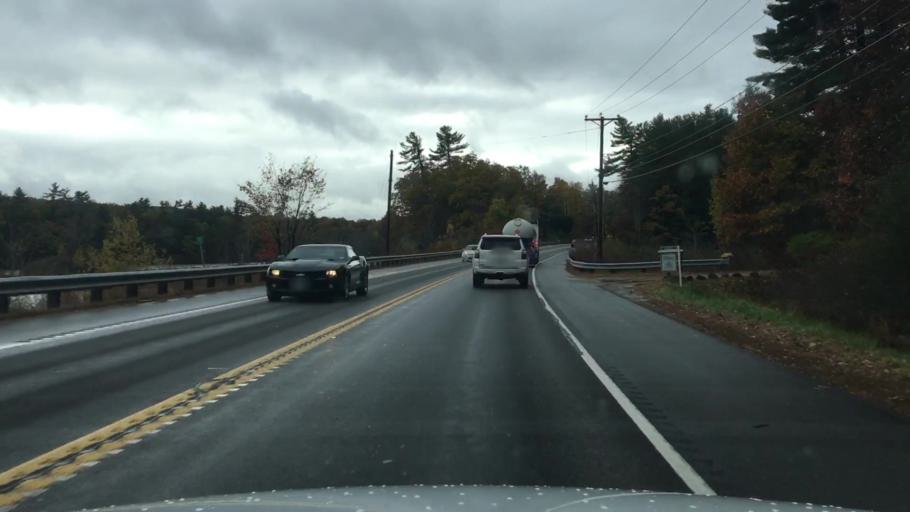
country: US
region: New Hampshire
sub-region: Strafford County
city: Lee
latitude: 43.1383
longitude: -71.0147
